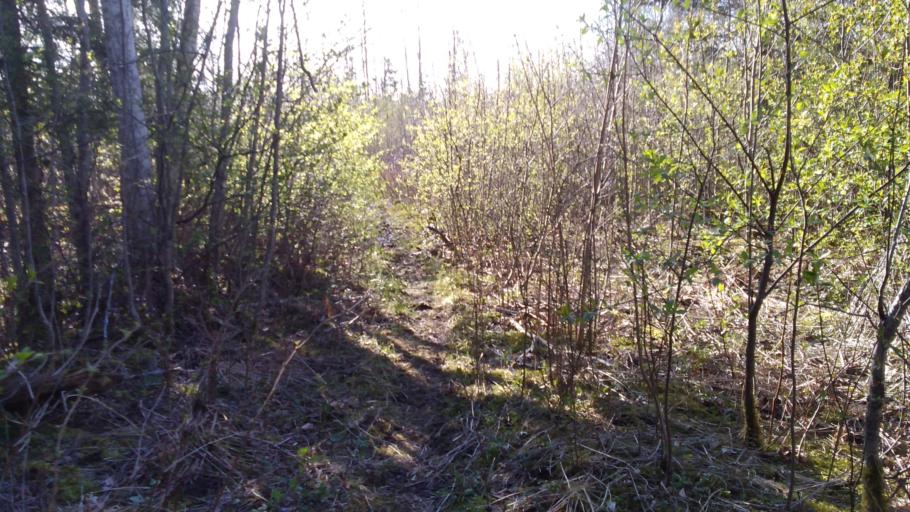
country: EE
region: Harju
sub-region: Saue linn
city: Saue
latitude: 59.2471
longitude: 24.5027
